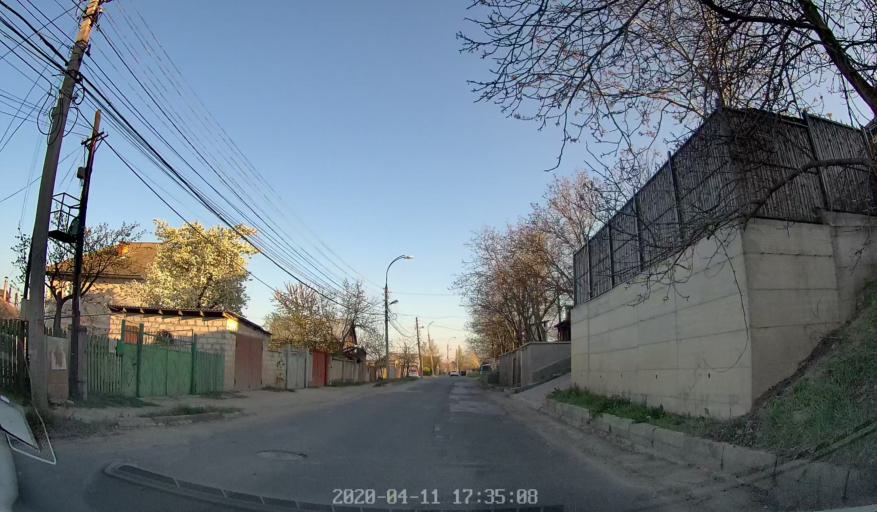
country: MD
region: Laloveni
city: Ialoveni
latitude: 46.9918
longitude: 28.8033
